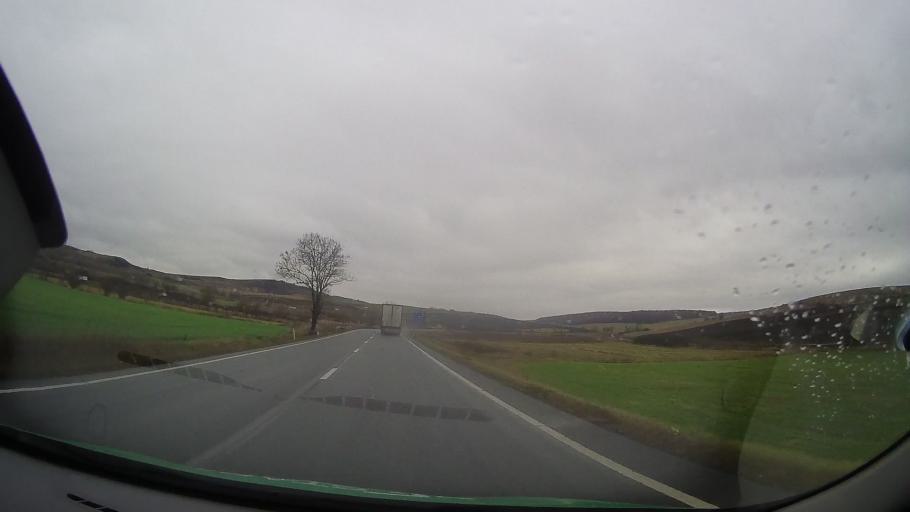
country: RO
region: Mures
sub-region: Comuna Lunca
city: Lunca
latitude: 46.8722
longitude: 24.5502
